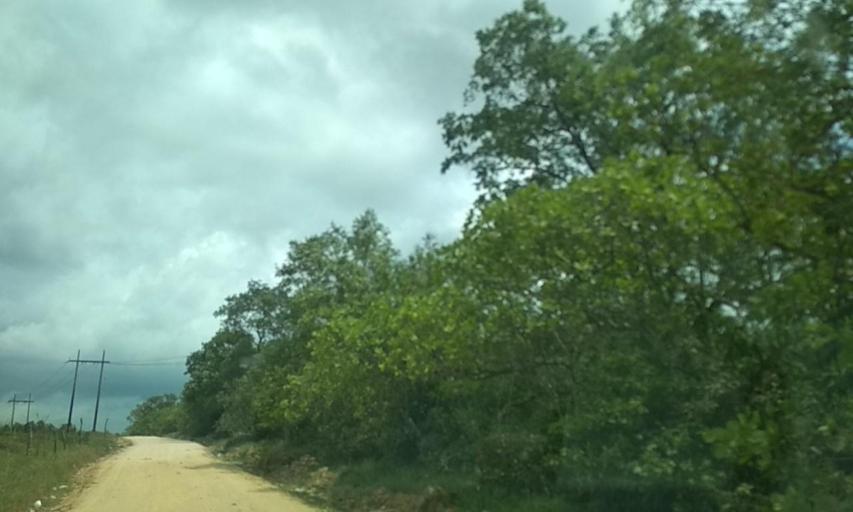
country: MX
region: Veracruz
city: Las Choapas
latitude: 17.9052
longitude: -94.1252
